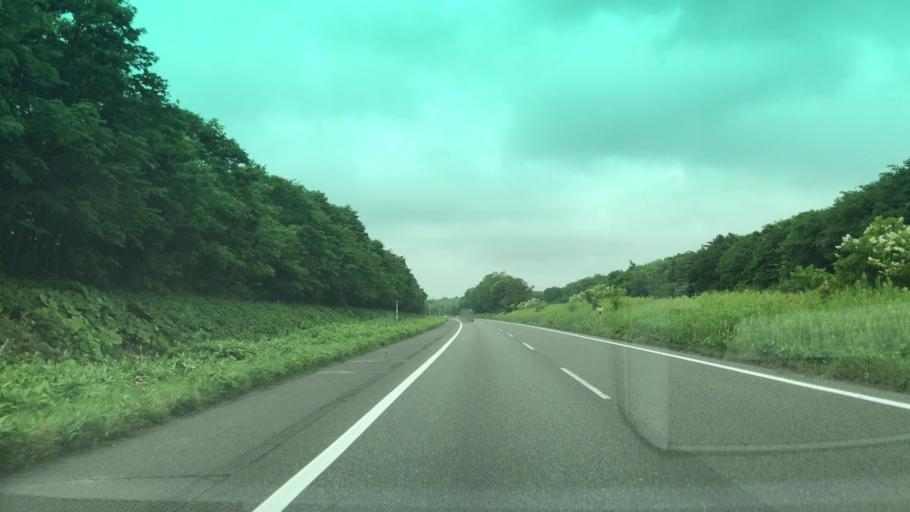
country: JP
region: Hokkaido
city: Chitose
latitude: 42.7407
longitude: 141.6510
